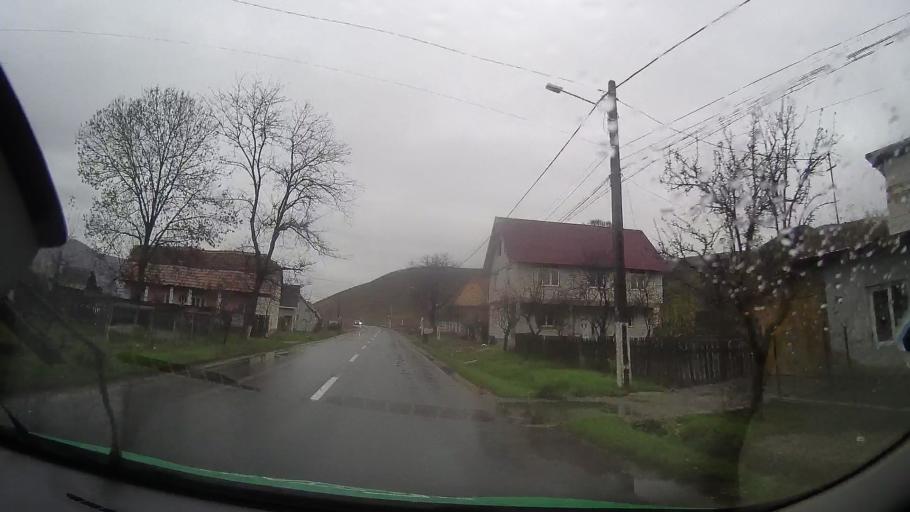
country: RO
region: Bistrita-Nasaud
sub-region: Comuna Mariselu
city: Mariselu
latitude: 47.0420
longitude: 24.4717
